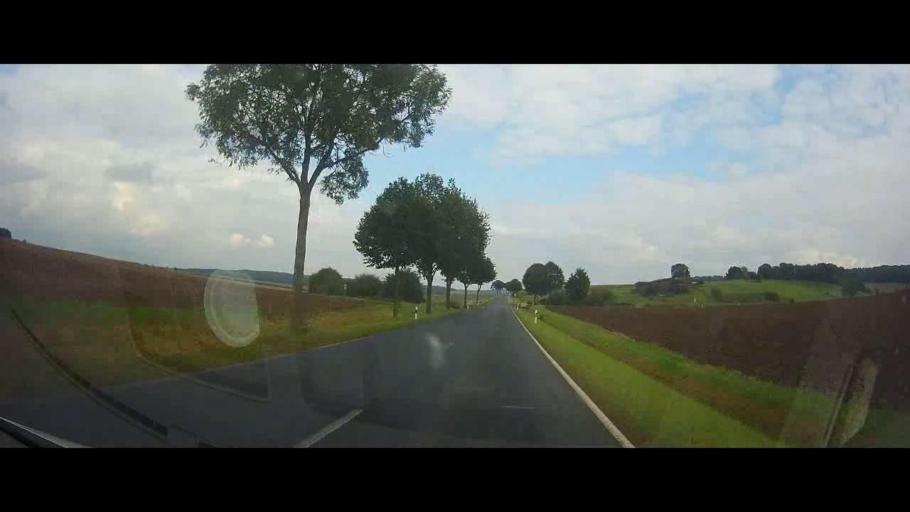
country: DE
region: Lower Saxony
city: Adelebsen
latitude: 51.5546
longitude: 9.7857
